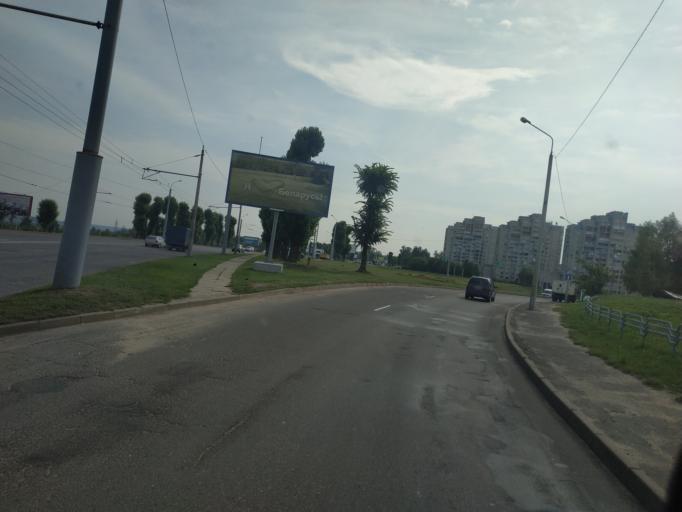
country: BY
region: Mogilev
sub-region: Mahilyowski Rayon
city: Veyno
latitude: 53.8771
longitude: 30.3811
